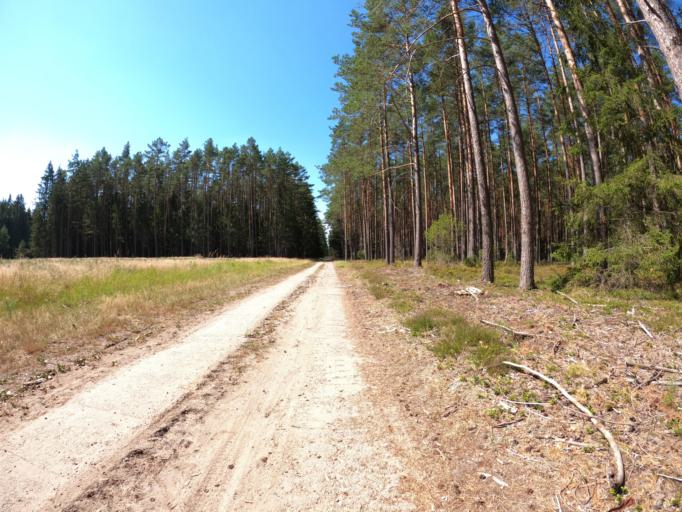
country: PL
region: West Pomeranian Voivodeship
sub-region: Powiat bialogardzki
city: Tychowo
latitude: 54.0514
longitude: 16.3350
